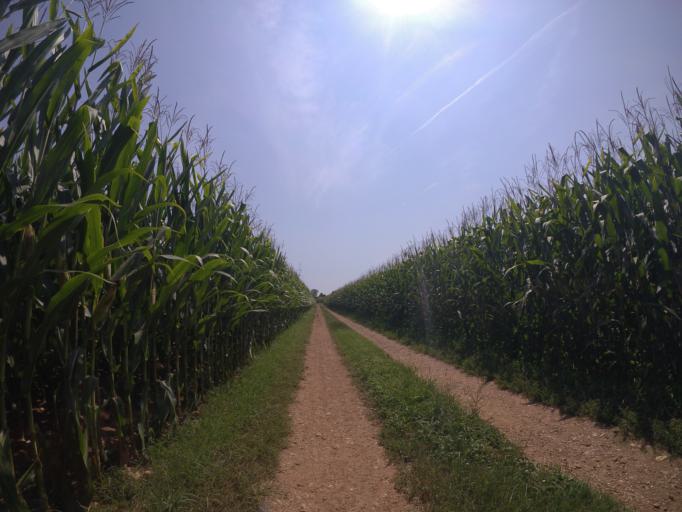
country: IT
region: Friuli Venezia Giulia
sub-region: Provincia di Udine
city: Bertiolo
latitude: 45.9425
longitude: 13.0765
